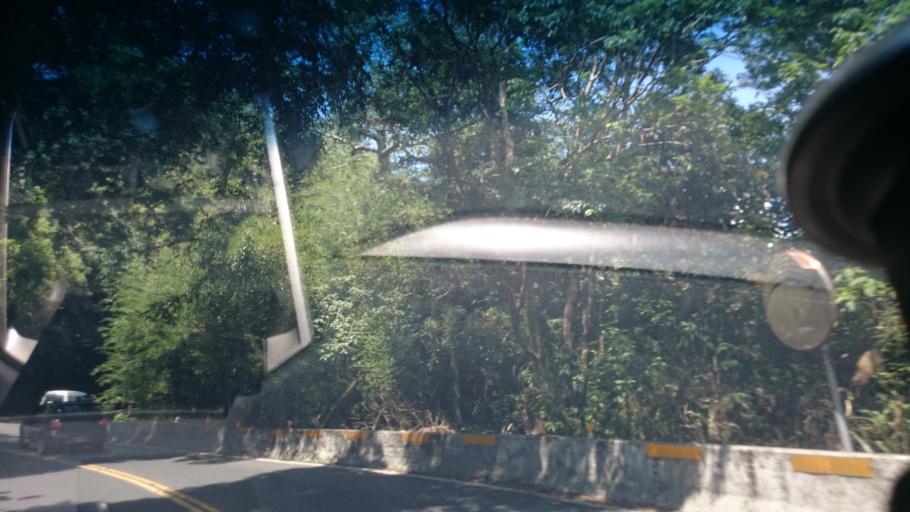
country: TW
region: Taiwan
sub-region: Nantou
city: Puli
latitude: 24.0254
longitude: 121.1374
